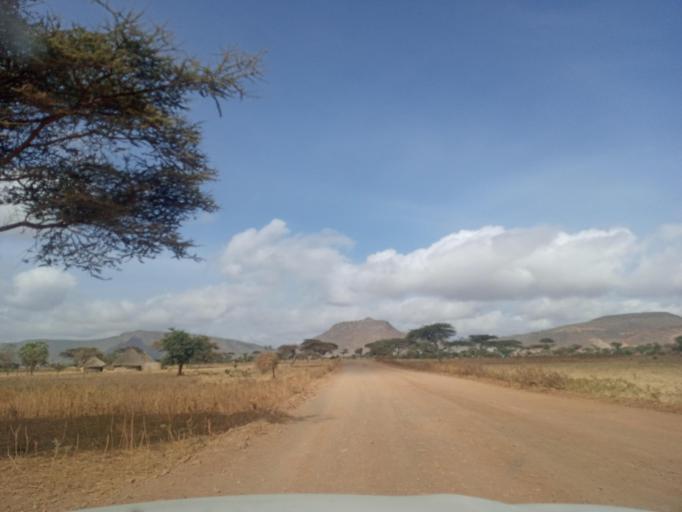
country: ET
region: Oromiya
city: Ziway
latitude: 7.9195
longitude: 38.6278
